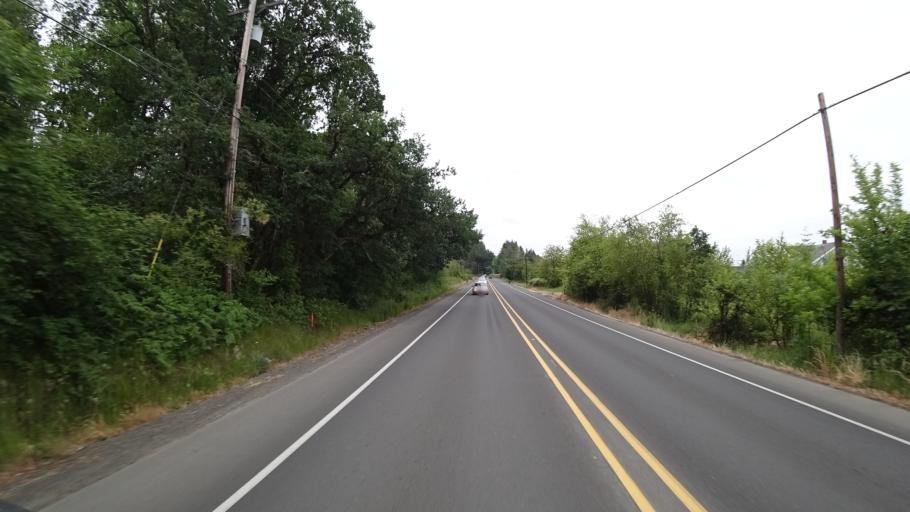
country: US
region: Oregon
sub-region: Washington County
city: Hillsboro
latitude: 45.4840
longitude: -122.9359
